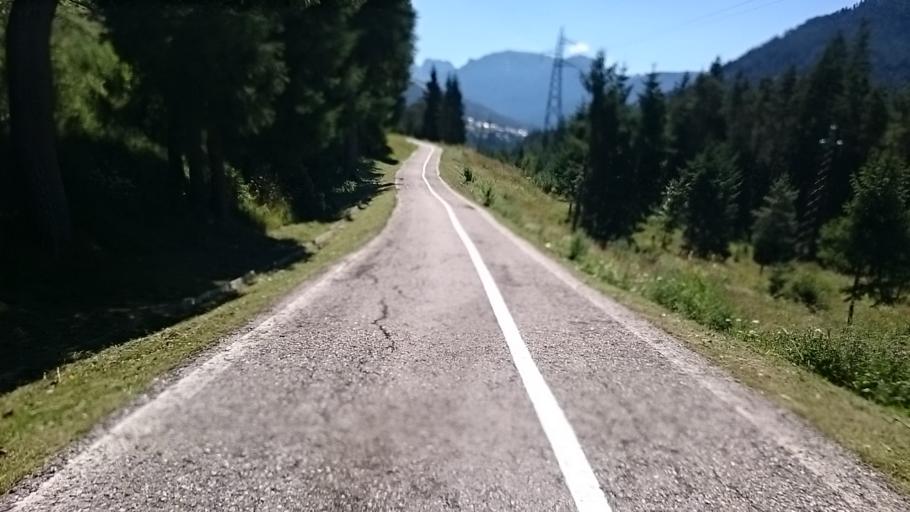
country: IT
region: Veneto
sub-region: Provincia di Belluno
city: San Vito
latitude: 46.4889
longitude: 12.1852
